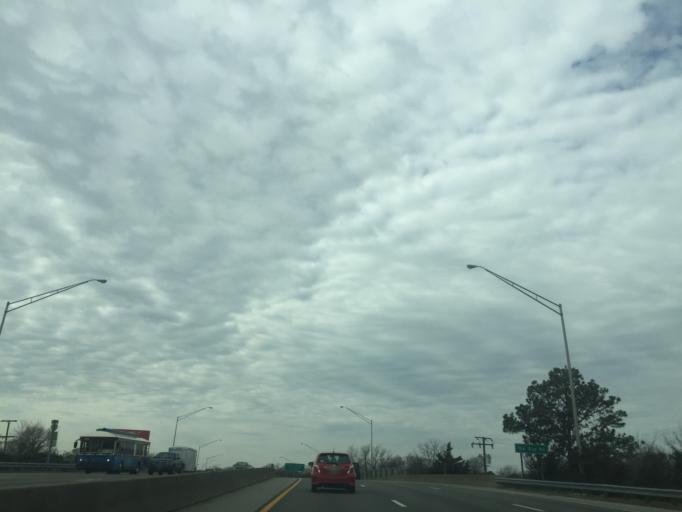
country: US
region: Virginia
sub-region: City of Hampton
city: Hampton
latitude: 37.0348
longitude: -76.3517
